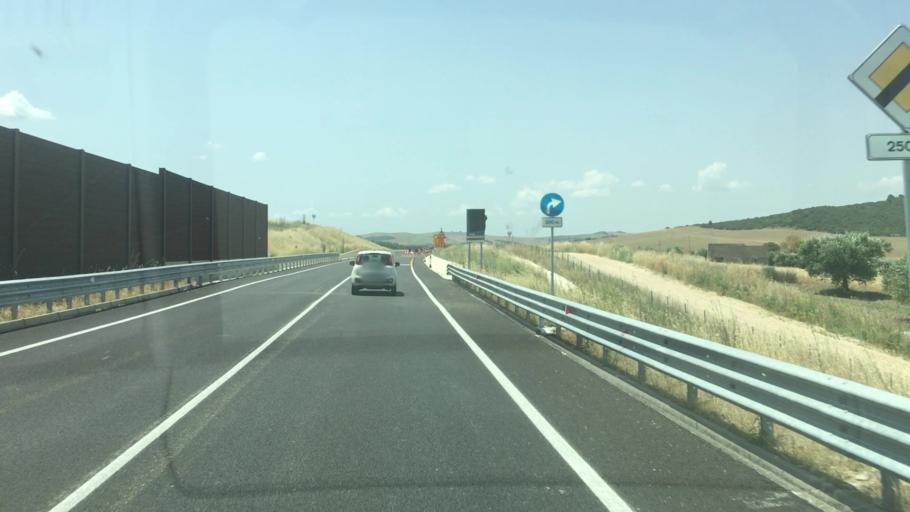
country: IT
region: Basilicate
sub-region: Provincia di Matera
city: La Martella
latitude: 40.6714
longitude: 16.4975
